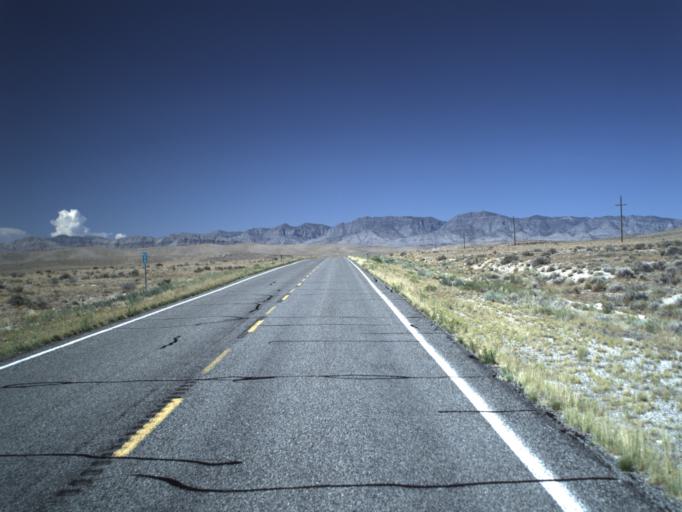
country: US
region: Utah
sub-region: Beaver County
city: Milford
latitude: 39.0468
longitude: -113.2828
